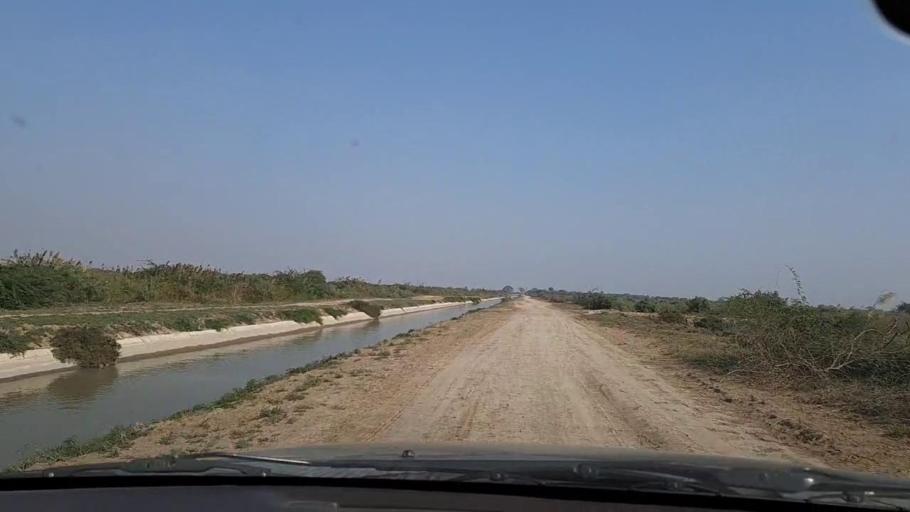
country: PK
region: Sindh
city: Mirpur Sakro
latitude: 24.3420
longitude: 67.7204
